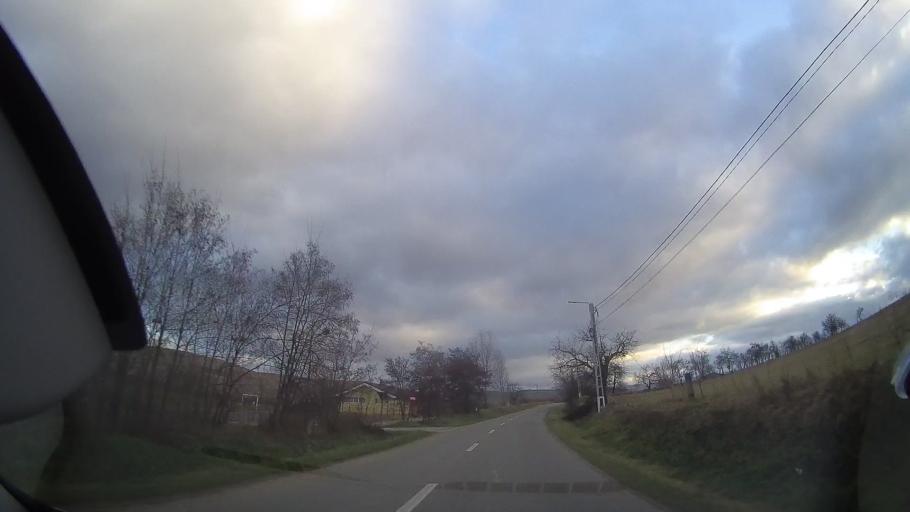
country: RO
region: Cluj
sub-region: Comuna Sancraiu
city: Sancraiu
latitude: 46.8252
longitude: 22.9909
